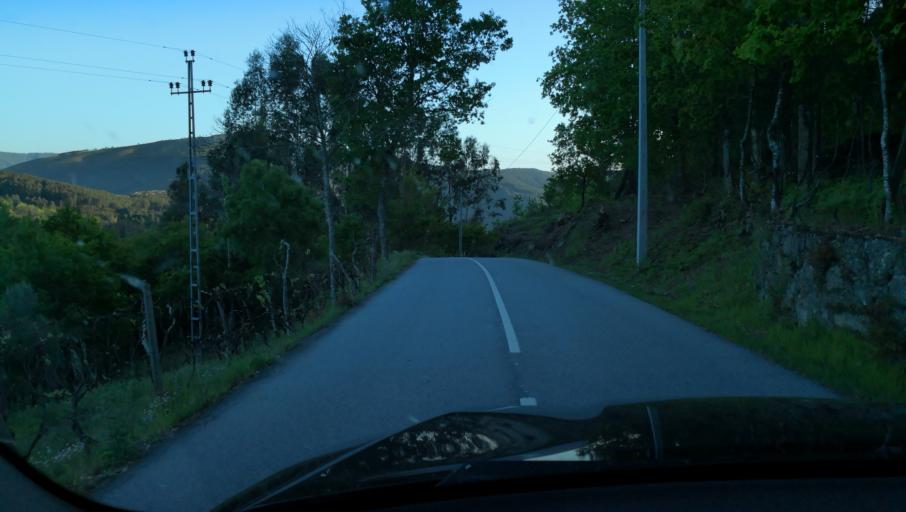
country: PT
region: Vila Real
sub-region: Mondim de Basto
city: Mondim de Basto
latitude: 41.4134
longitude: -7.8962
